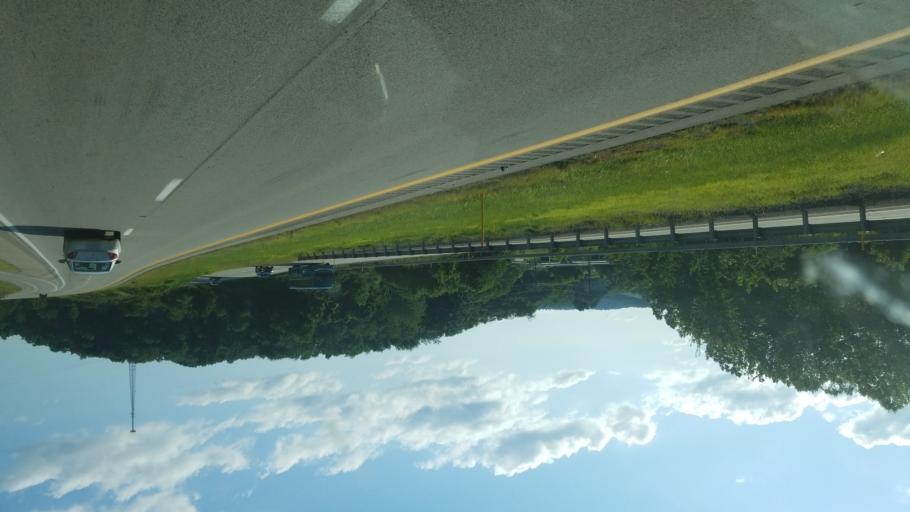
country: US
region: Pennsylvania
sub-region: Greene County
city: Waynesburg
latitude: 39.9577
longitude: -80.1702
